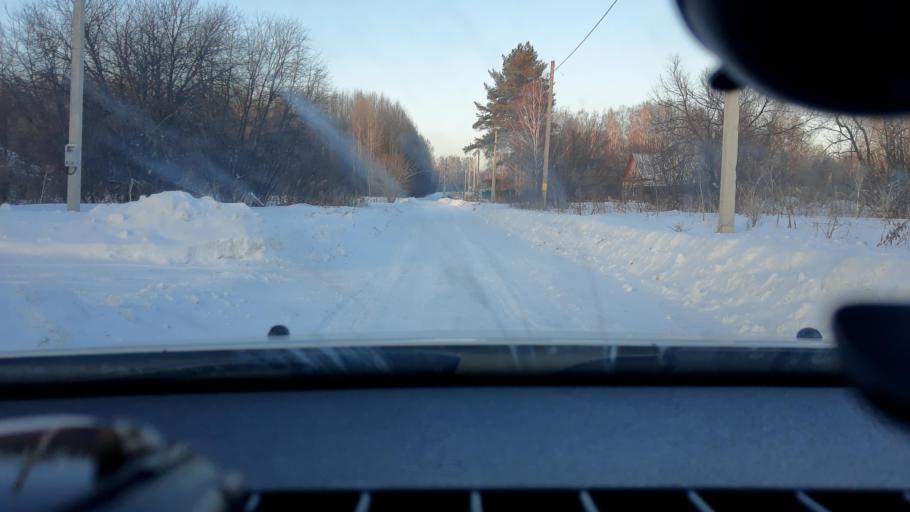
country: RU
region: Bashkortostan
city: Kudeyevskiy
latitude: 54.7988
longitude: 56.6753
